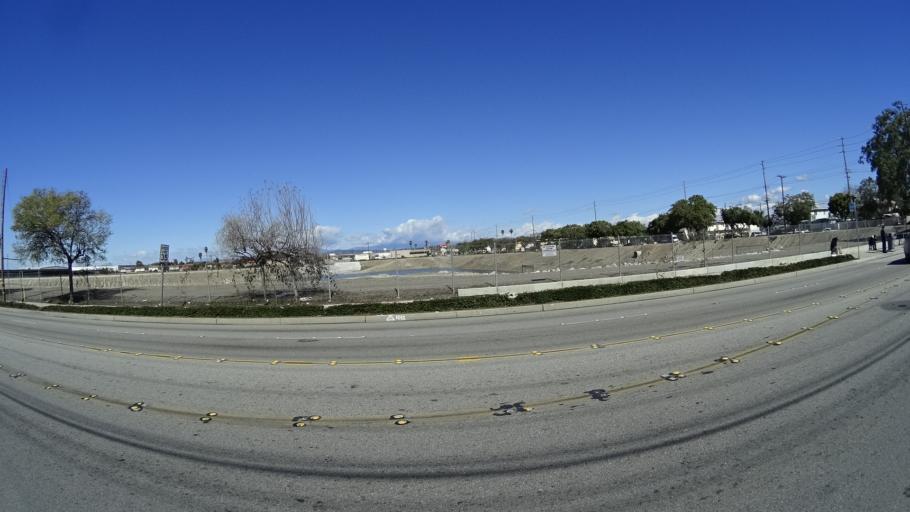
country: US
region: California
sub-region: Orange County
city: Anaheim
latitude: 33.8472
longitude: -117.9068
